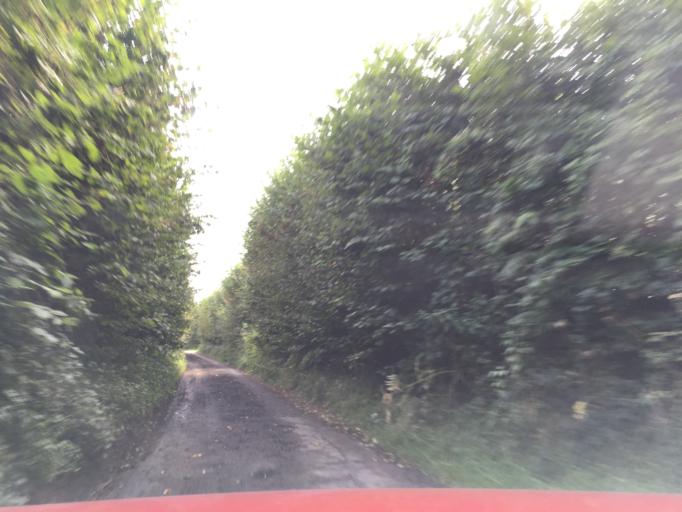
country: GB
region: England
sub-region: South Gloucestershire
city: Tytherington
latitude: 51.6062
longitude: -2.4592
